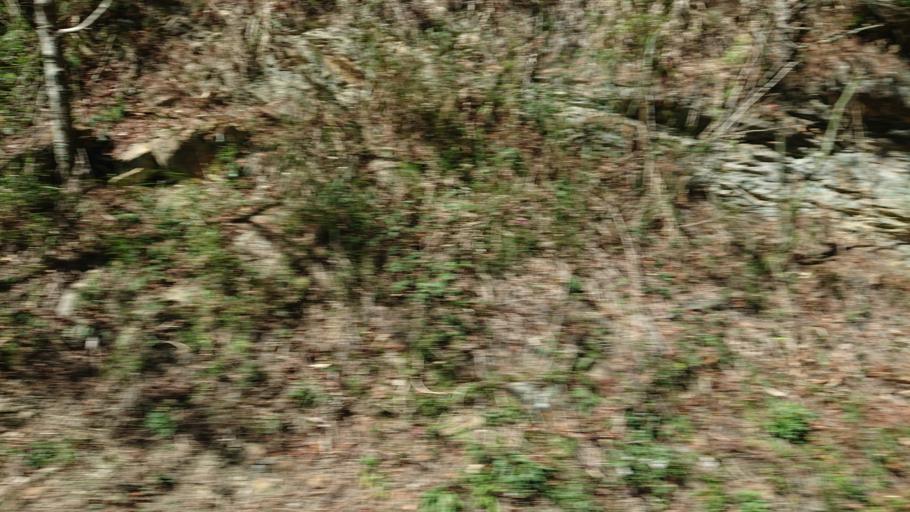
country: TW
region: Taiwan
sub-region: Hualien
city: Hualian
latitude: 24.3472
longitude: 121.3099
